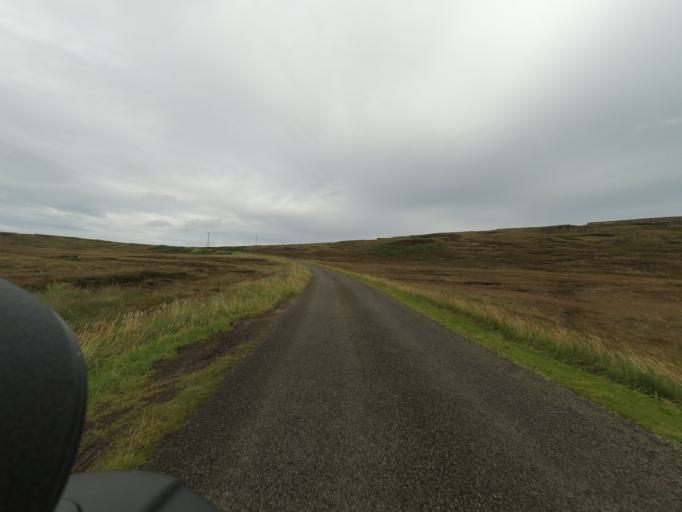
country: GB
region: Scotland
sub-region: Highland
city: Thurso
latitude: 58.6675
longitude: -3.3749
